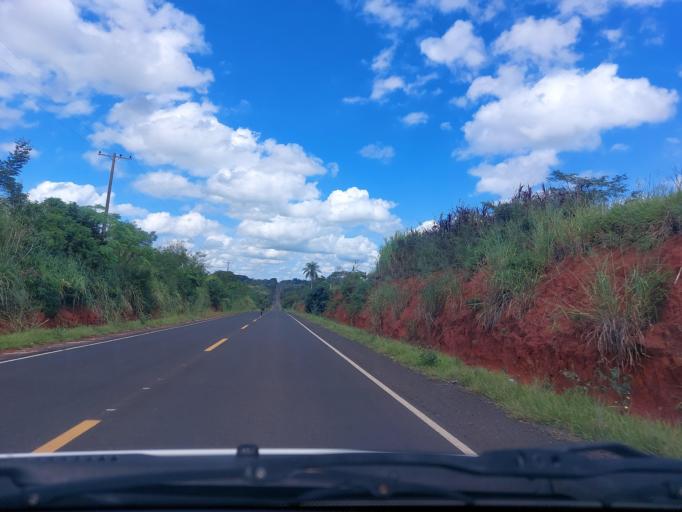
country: PY
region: San Pedro
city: Guayaybi
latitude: -24.5431
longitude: -56.5196
